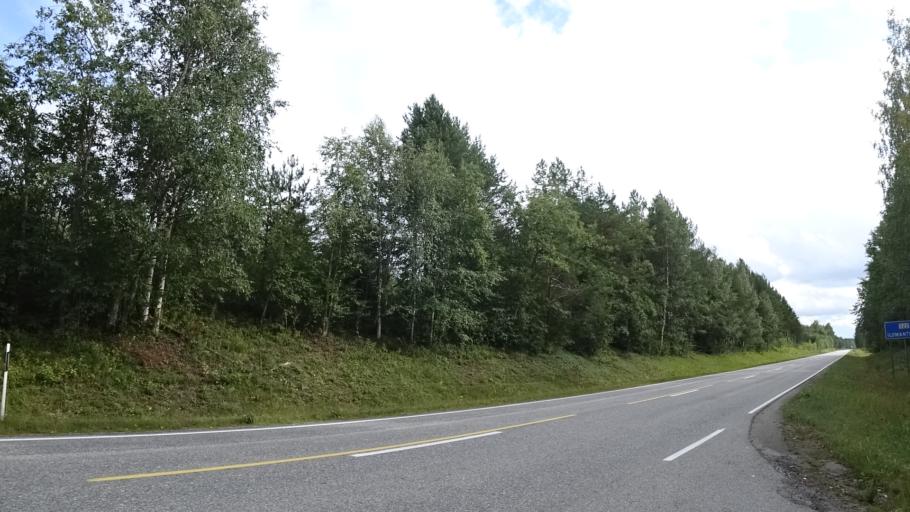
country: FI
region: North Karelia
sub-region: Joensuu
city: Ilomantsi
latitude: 62.7431
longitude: 30.9961
